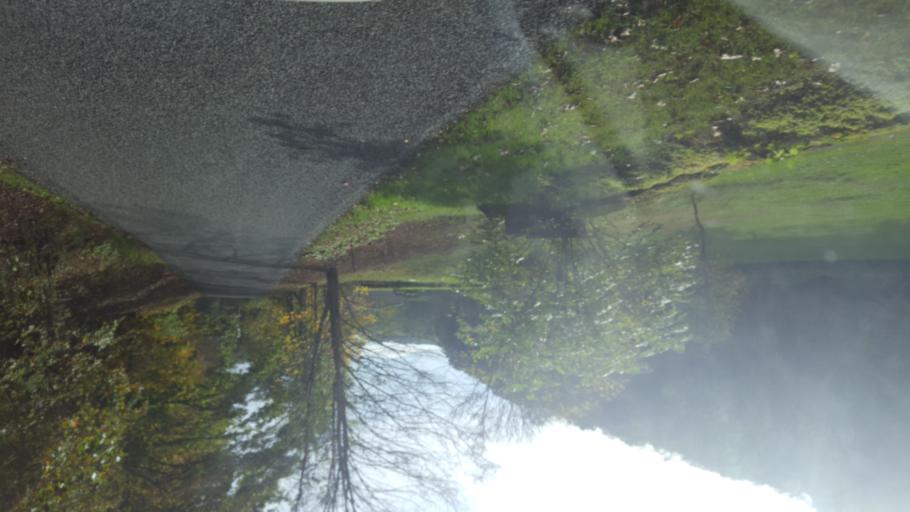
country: US
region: Ohio
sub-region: Holmes County
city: Millersburg
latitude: 40.5339
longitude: -81.8633
